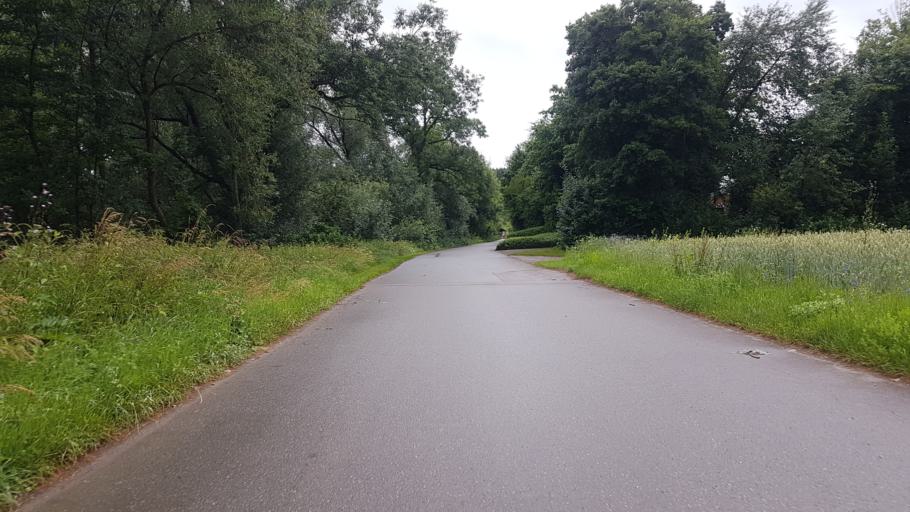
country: DE
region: Baden-Wuerttemberg
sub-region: Tuebingen Region
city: Rottenacker
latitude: 48.2361
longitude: 9.7045
